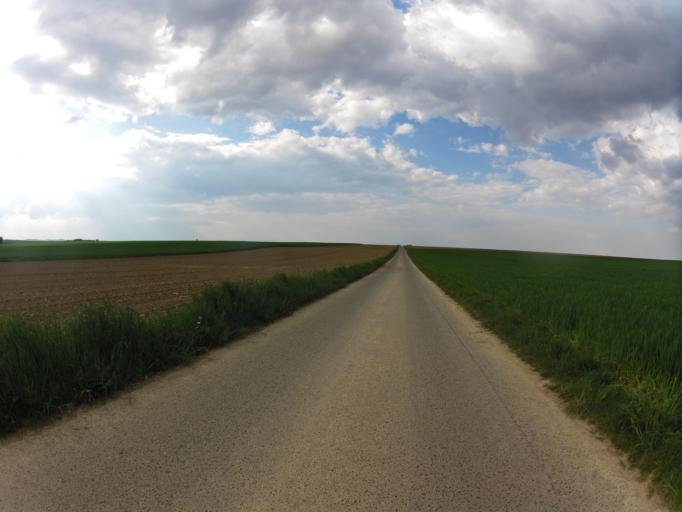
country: DE
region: Bavaria
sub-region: Regierungsbezirk Unterfranken
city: Giebelstadt
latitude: 49.6360
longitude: 9.9400
